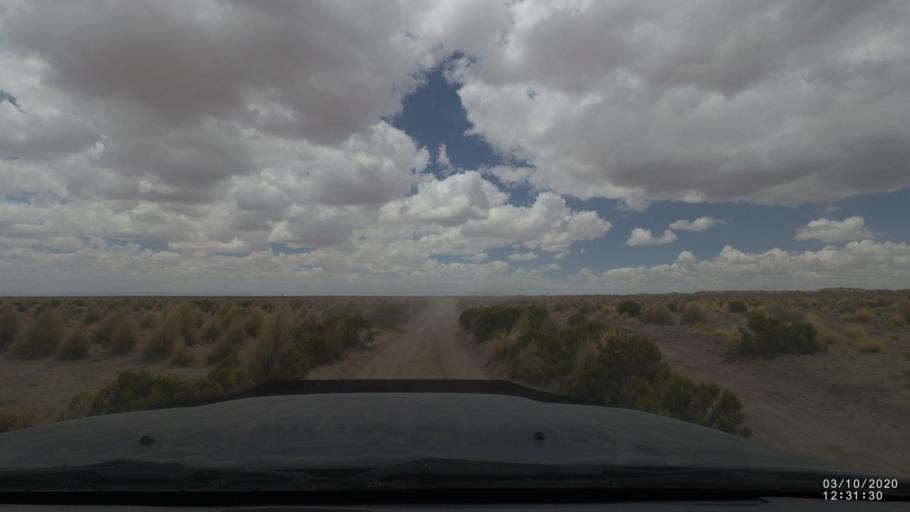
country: BO
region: Oruro
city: Poopo
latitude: -18.6866
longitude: -67.5388
